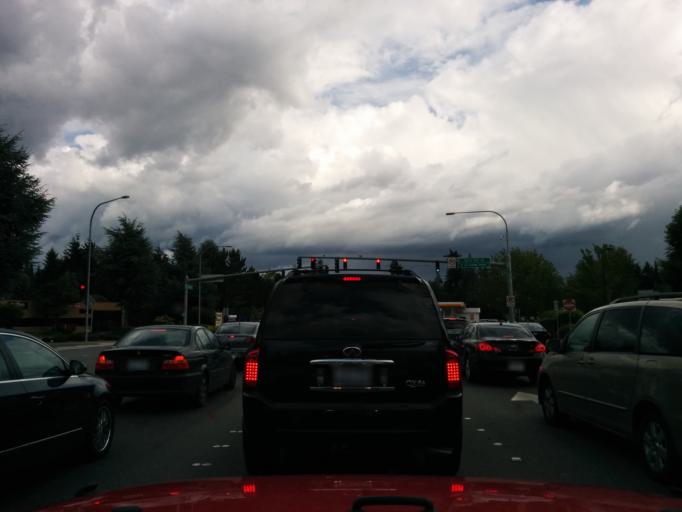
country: US
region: Washington
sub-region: King County
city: Redmond
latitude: 47.6664
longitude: -122.1007
